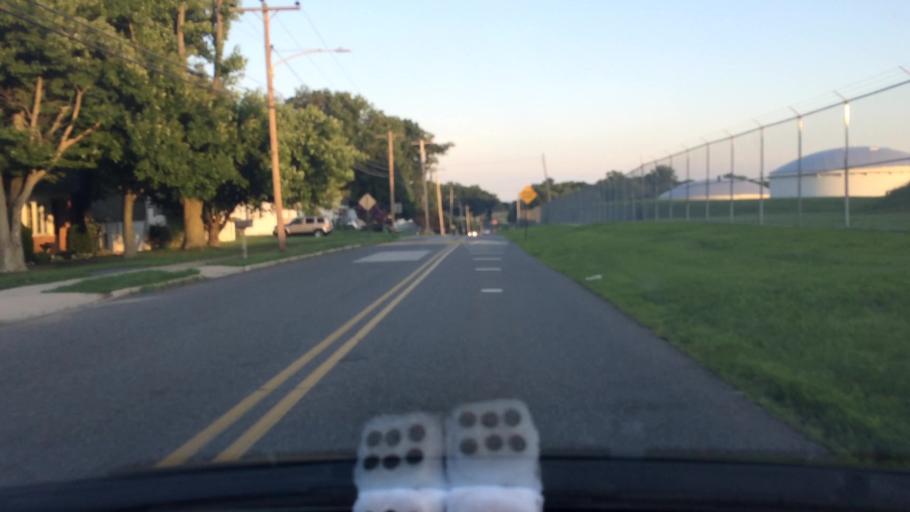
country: US
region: Pennsylvania
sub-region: Delaware County
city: Village Green-Green Ridge
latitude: 39.8673
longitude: -75.4534
